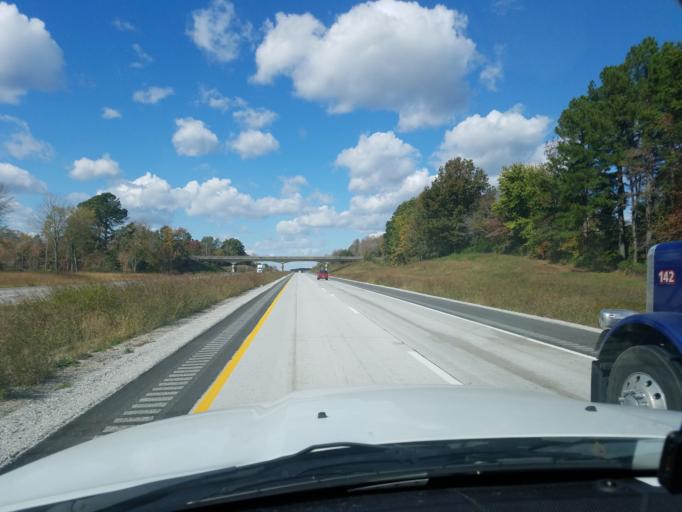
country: US
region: Kentucky
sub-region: Ohio County
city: Oak Grove
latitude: 37.3363
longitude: -86.7605
